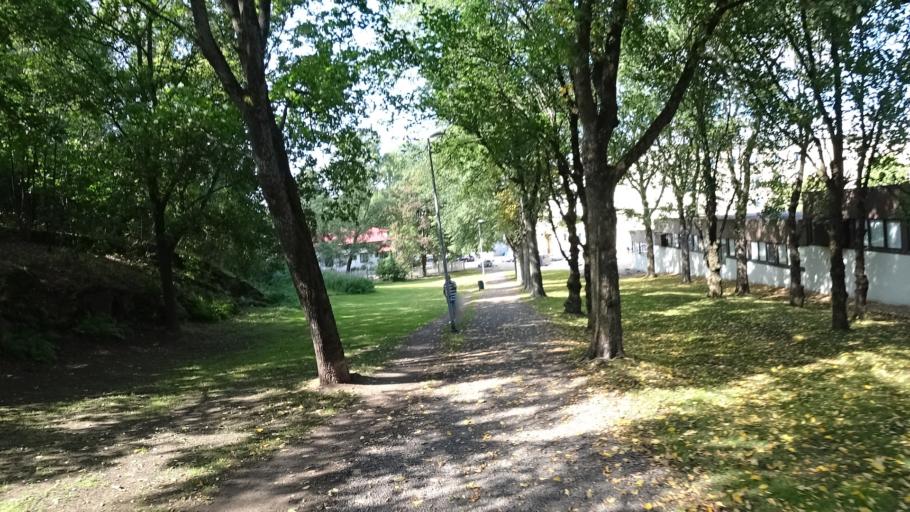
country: FI
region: Kymenlaakso
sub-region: Kotka-Hamina
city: Kotka
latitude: 60.4618
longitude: 26.9334
